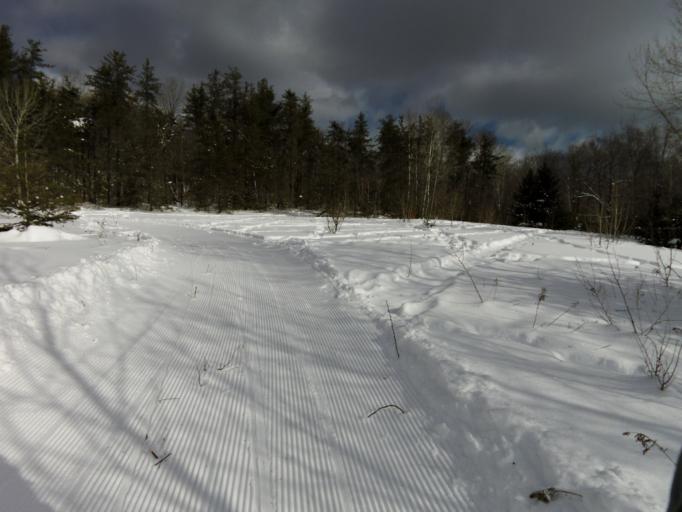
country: CA
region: Quebec
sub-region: Outaouais
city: Wakefield
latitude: 45.5266
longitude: -75.8620
